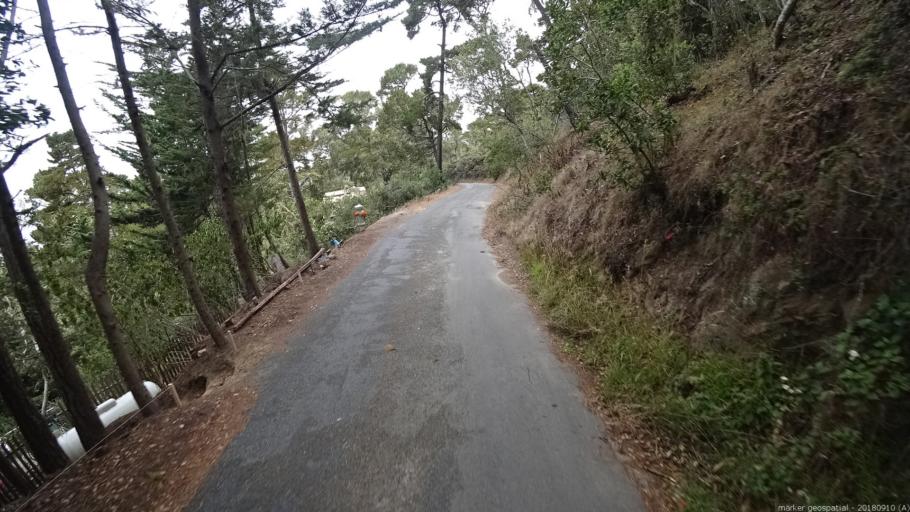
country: US
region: California
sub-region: Monterey County
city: Carmel-by-the-Sea
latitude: 36.5006
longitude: -121.9313
